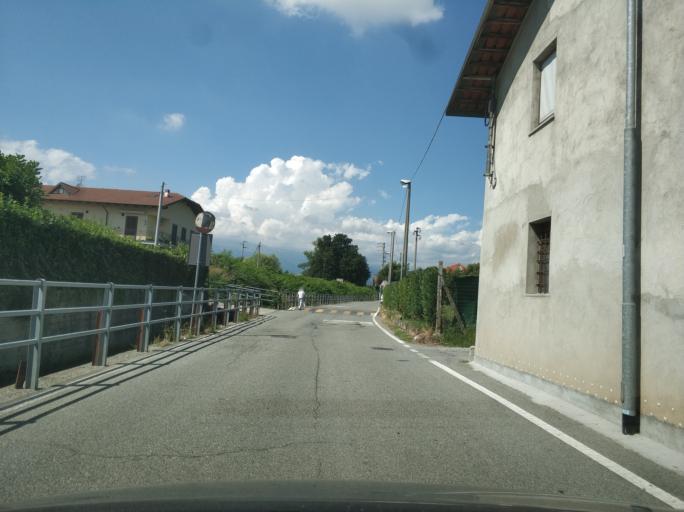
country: IT
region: Piedmont
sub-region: Provincia di Torino
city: Rivarolo Canavese
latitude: 45.3221
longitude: 7.7201
